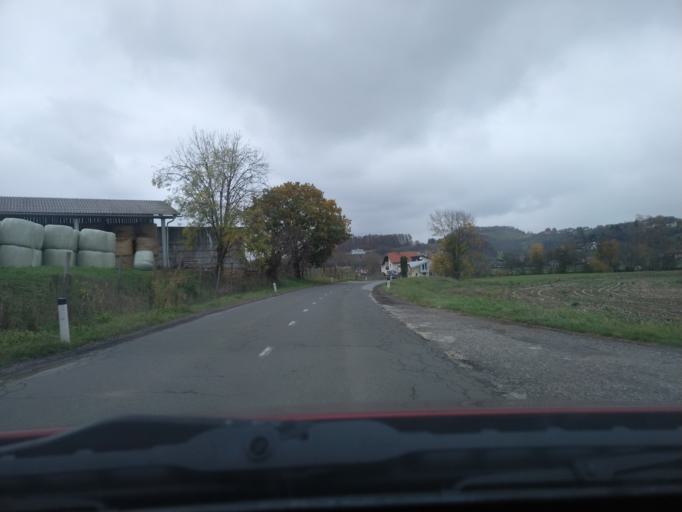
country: SI
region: Pesnica
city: Pesnica pri Mariboru
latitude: 46.5995
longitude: 15.6564
